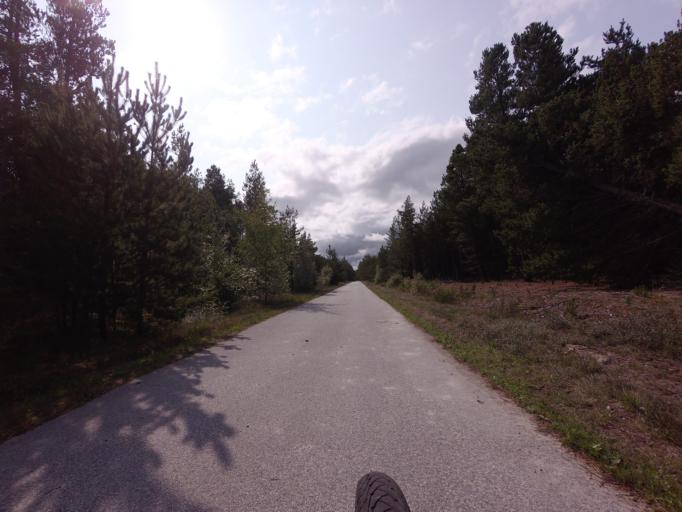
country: DK
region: North Denmark
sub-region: Frederikshavn Kommune
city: Strandby
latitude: 57.6408
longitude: 10.4412
